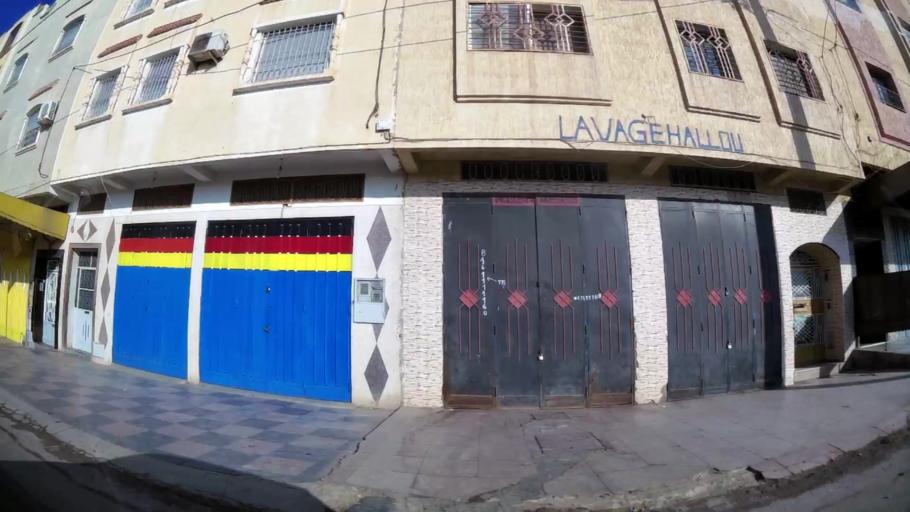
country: MA
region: Oriental
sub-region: Oujda-Angad
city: Oujda
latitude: 34.6736
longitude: -1.9395
